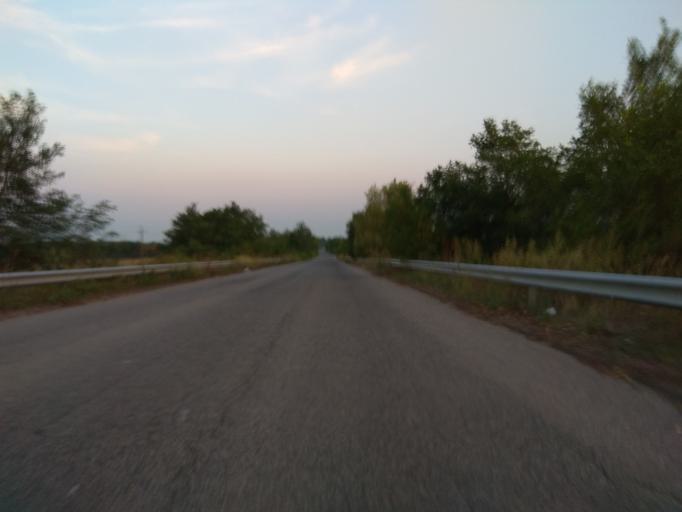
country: HU
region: Borsod-Abauj-Zemplen
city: Emod
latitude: 47.9164
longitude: 20.8460
